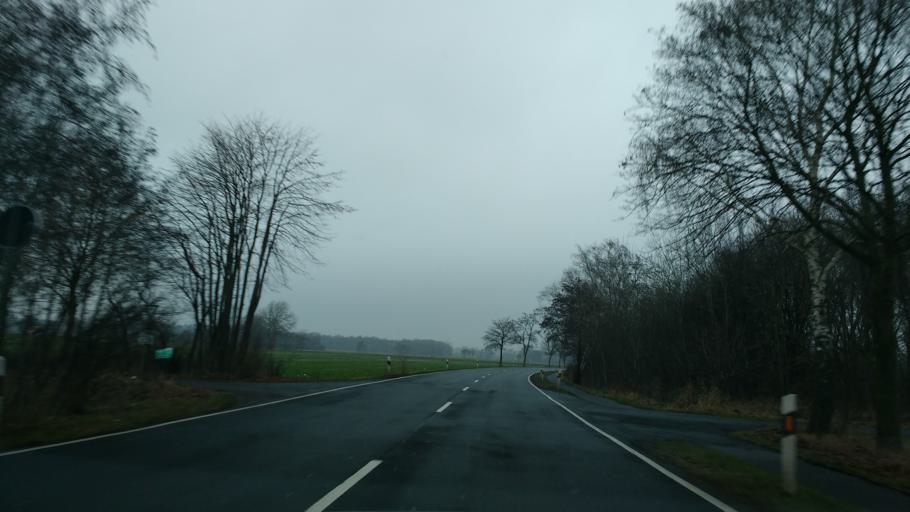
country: DE
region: Lower Saxony
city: Garbsen
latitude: 52.4263
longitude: 9.5725
